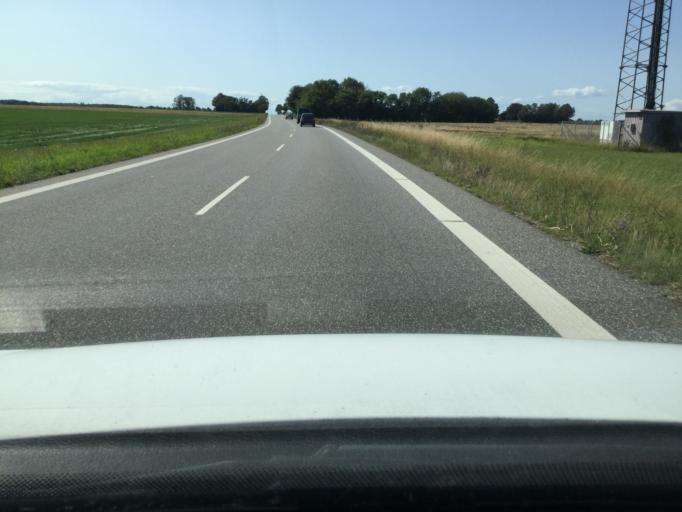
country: DK
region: Zealand
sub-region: Lolland Kommune
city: Nakskov
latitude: 54.8029
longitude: 11.2691
